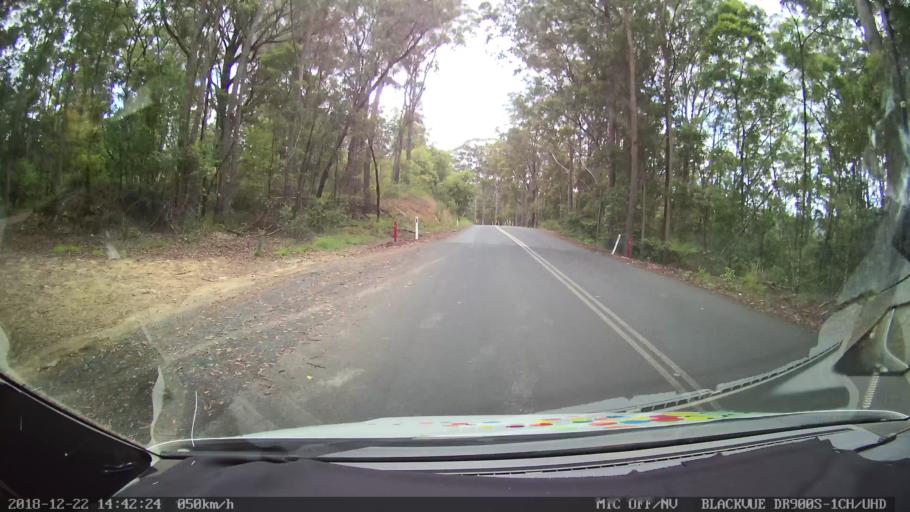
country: AU
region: New South Wales
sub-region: Bellingen
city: Dorrigo
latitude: -30.1590
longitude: 152.5842
